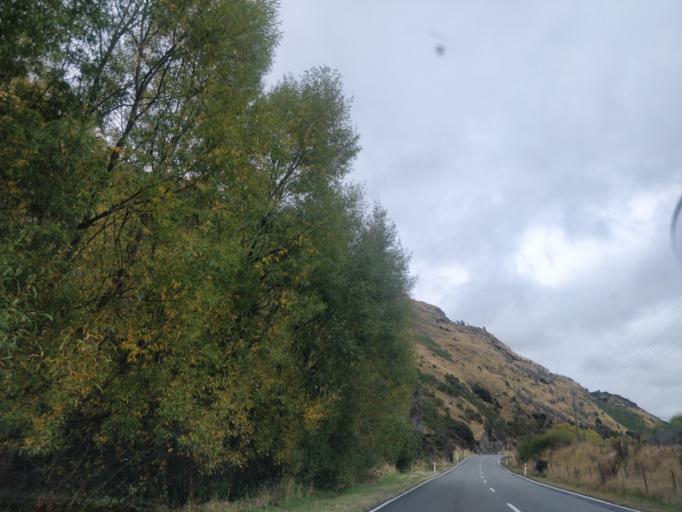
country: NZ
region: Canterbury
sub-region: Waimakariri District
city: Oxford
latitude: -43.0118
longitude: 171.7213
